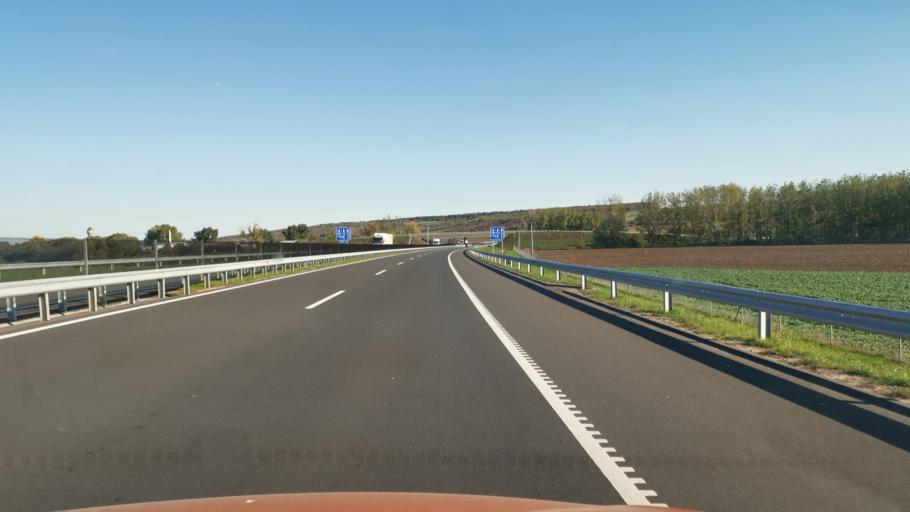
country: HU
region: Borsod-Abauj-Zemplen
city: Szikszo
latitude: 48.2049
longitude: 20.9109
